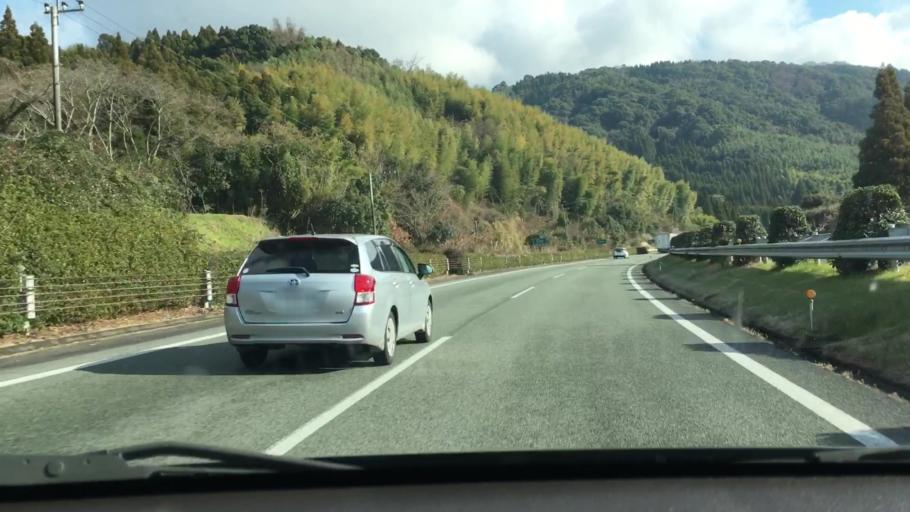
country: JP
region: Kumamoto
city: Matsubase
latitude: 32.6166
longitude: 130.7210
